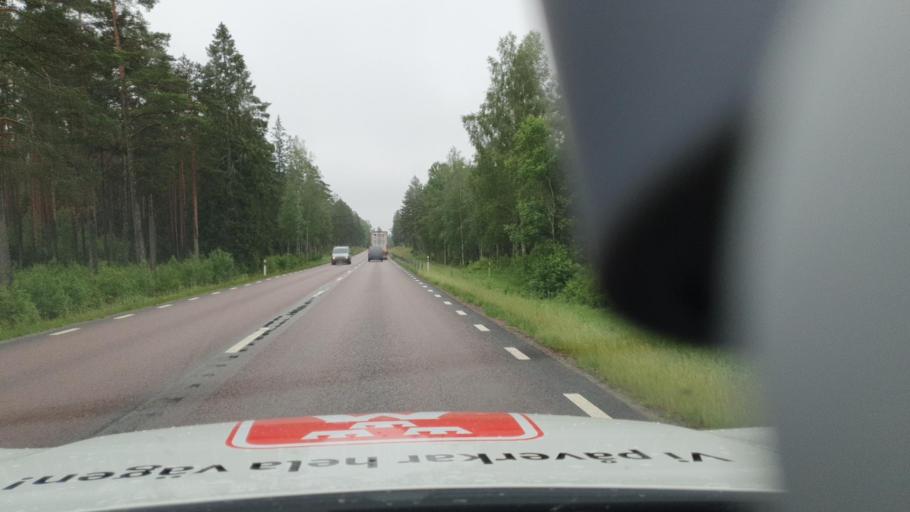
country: SE
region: Vaermland
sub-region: Kristinehamns Kommun
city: Bjorneborg
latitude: 59.2020
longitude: 14.1829
